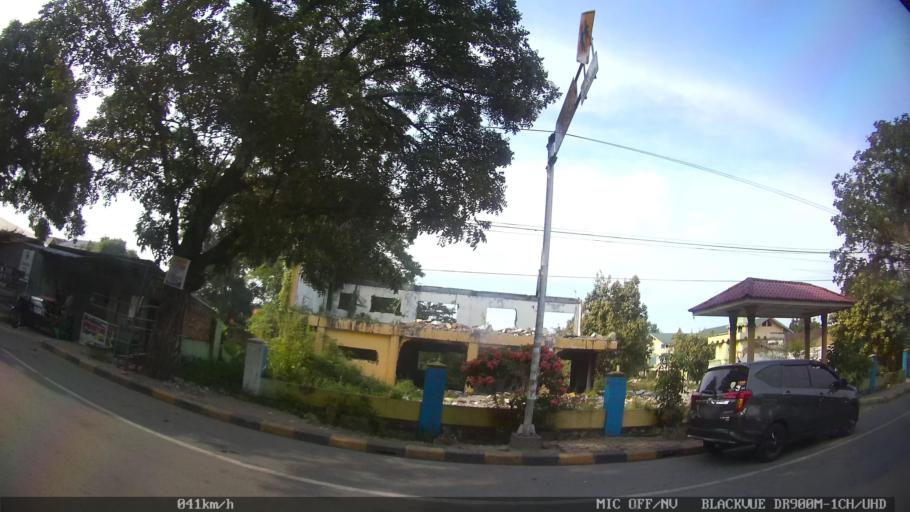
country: ID
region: North Sumatra
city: Binjai
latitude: 3.6085
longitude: 98.4958
